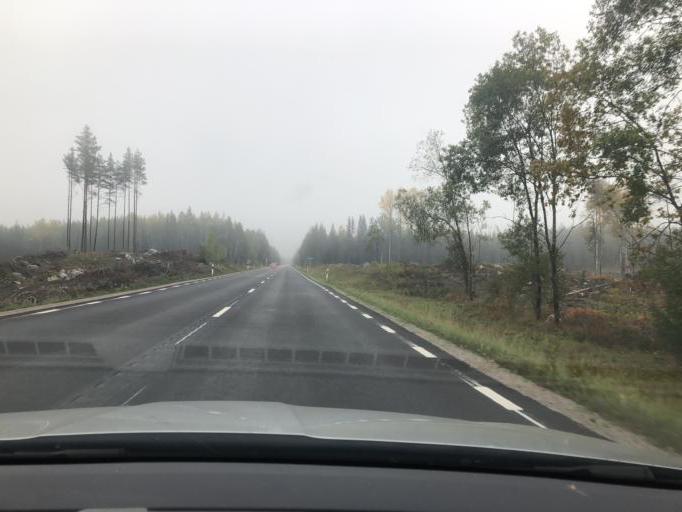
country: SE
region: Uppsala
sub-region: Tierps Kommun
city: Orbyhus
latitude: 60.2368
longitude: 17.6671
